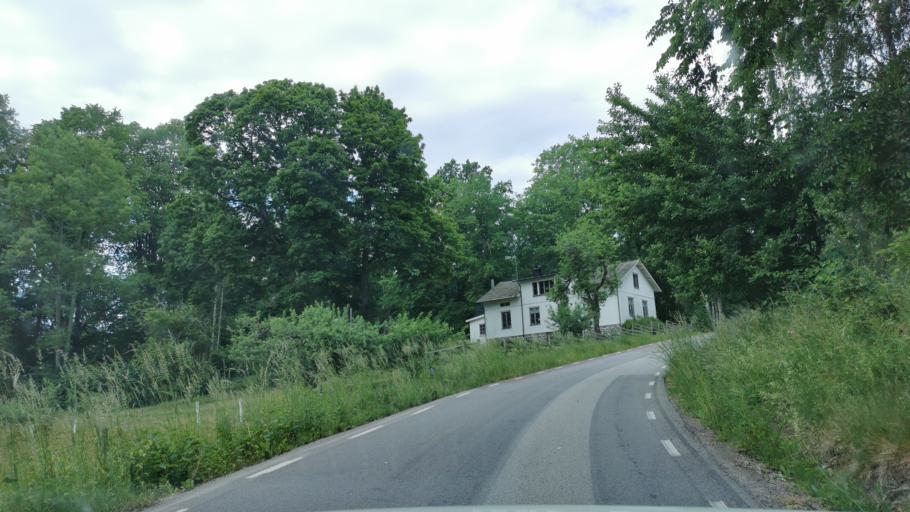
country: SE
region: Vaestra Goetaland
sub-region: Bengtsfors Kommun
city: Dals Langed
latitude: 58.8457
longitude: 12.4078
